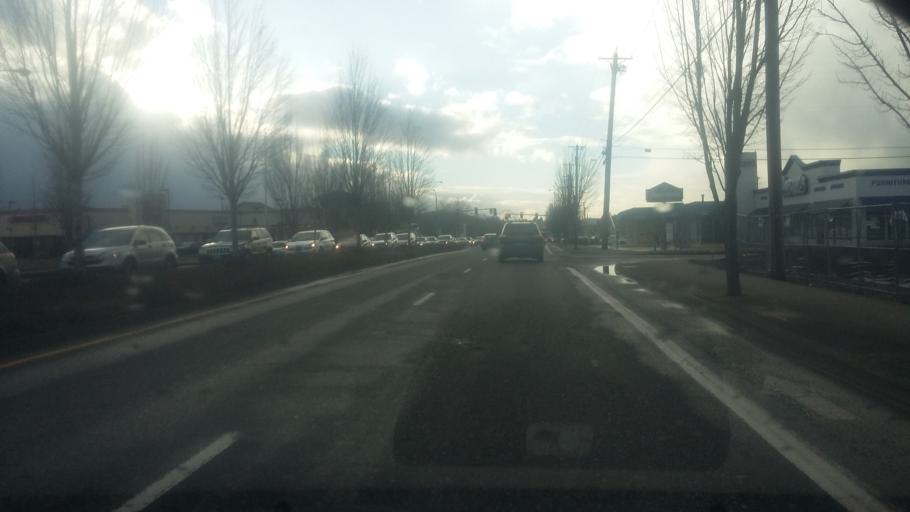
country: US
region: Oregon
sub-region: Washington County
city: Beaverton
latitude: 45.4905
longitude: -122.7934
